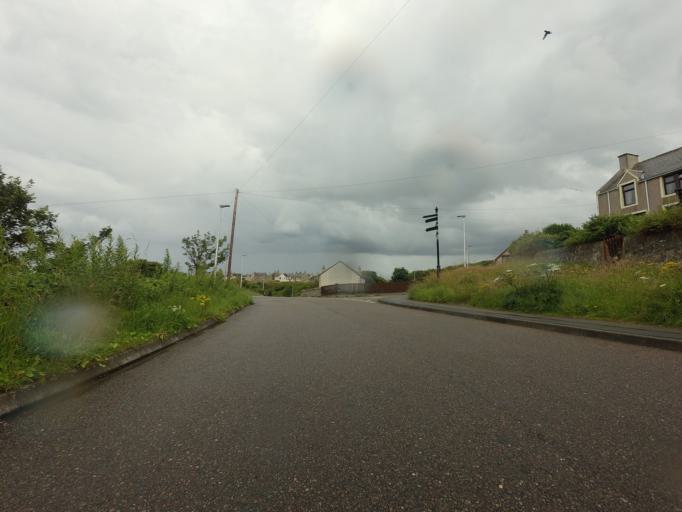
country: GB
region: Scotland
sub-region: Moray
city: Buckie
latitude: 57.6755
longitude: -2.9764
